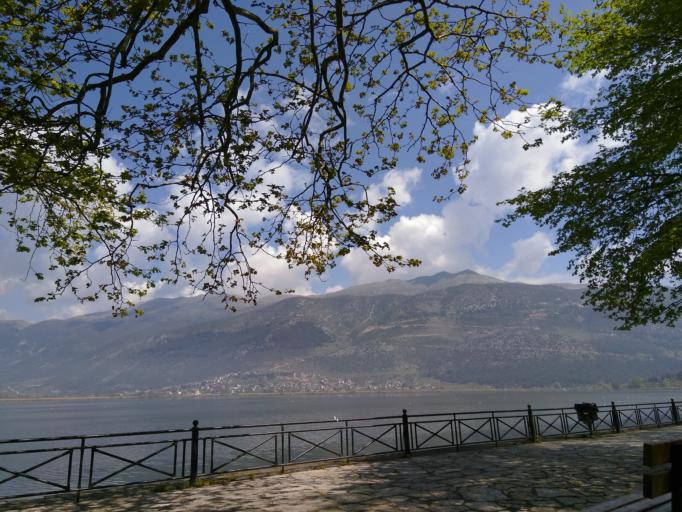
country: GR
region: Epirus
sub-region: Nomos Ioanninon
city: Ioannina
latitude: 39.6739
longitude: 20.8591
